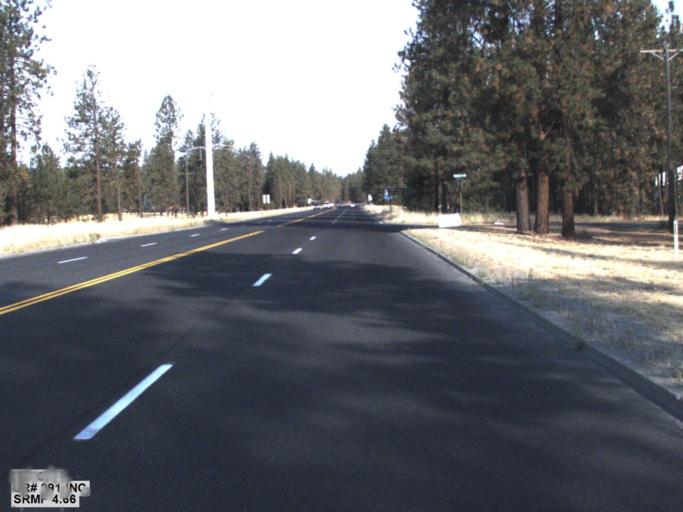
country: US
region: Washington
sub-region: Spokane County
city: Town and Country
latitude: 47.7305
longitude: -117.5017
